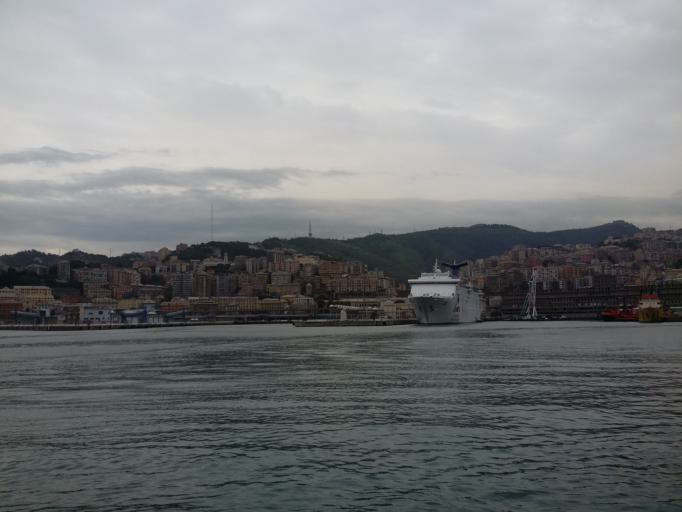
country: IT
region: Liguria
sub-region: Provincia di Genova
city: San Teodoro
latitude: 44.4080
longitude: 8.9188
